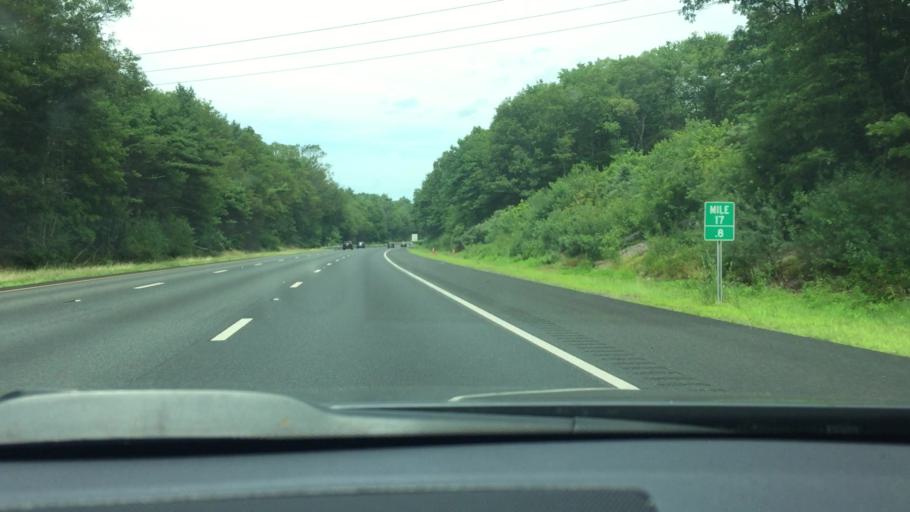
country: US
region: Massachusetts
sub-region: Norfolk County
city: Walpole
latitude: 42.1093
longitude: -71.2308
